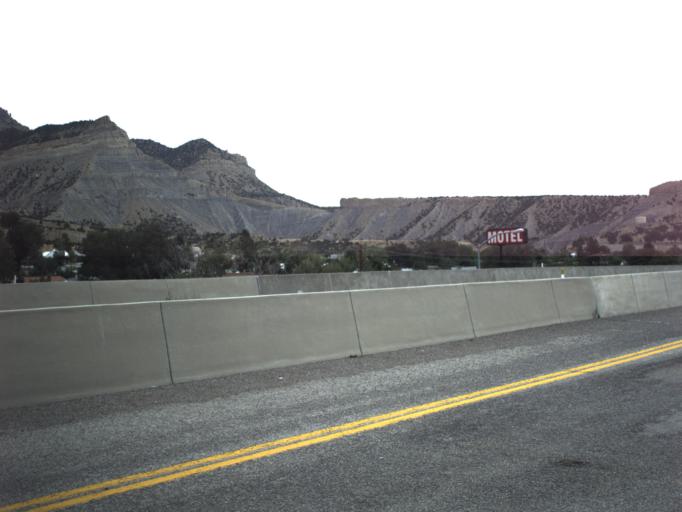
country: US
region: Utah
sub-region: Carbon County
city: Helper
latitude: 39.6919
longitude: -110.8582
